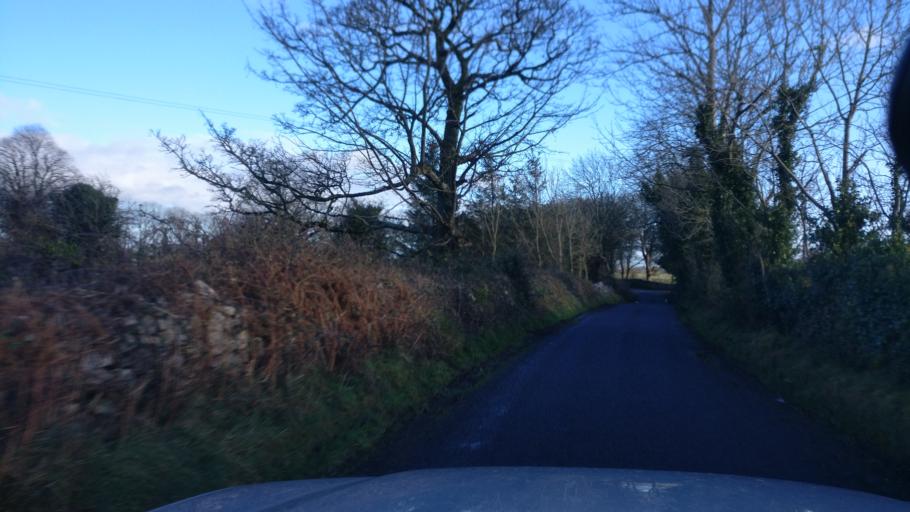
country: IE
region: Connaught
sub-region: County Galway
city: Loughrea
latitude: 53.2294
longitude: -8.5708
